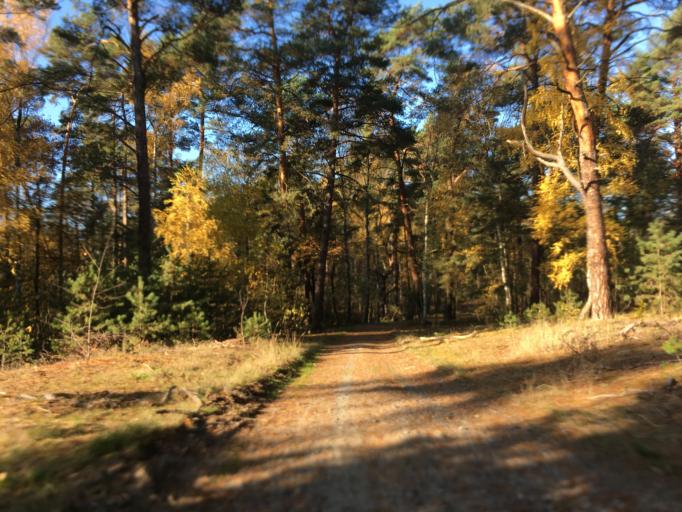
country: DE
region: Brandenburg
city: Wendisch Rietz
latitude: 52.1836
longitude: 13.9994
